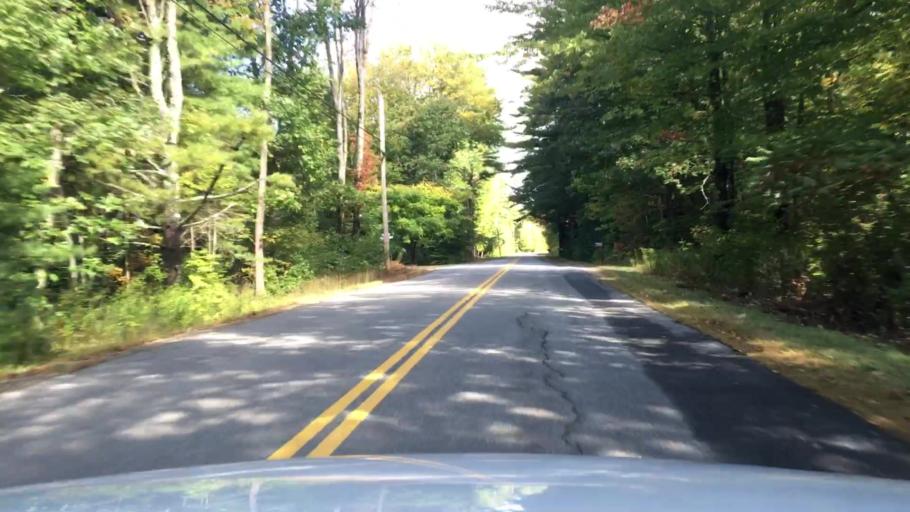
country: US
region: Maine
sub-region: Cumberland County
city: Brunswick
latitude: 43.9448
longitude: -69.8977
